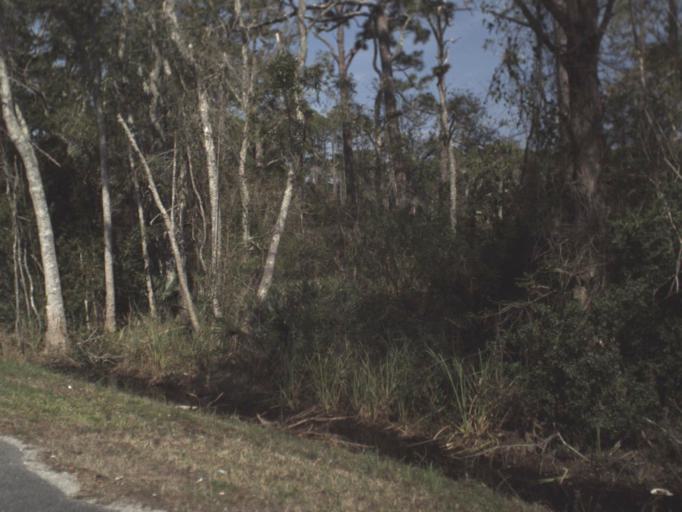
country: US
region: Florida
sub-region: Franklin County
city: Carrabelle
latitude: 29.8371
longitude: -84.6822
